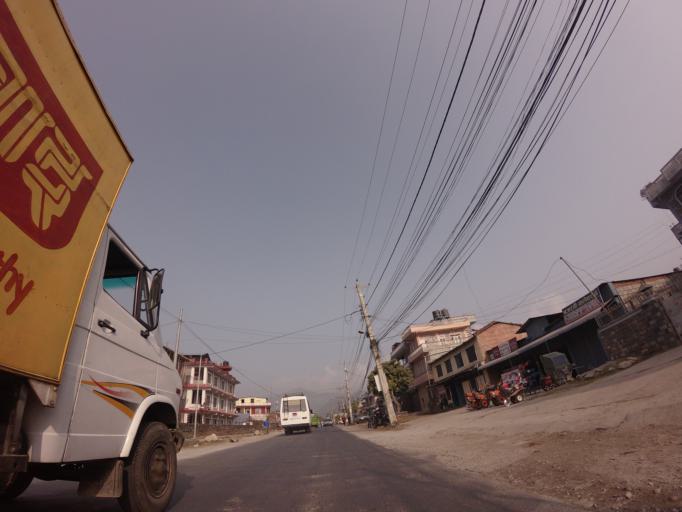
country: NP
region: Western Region
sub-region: Gandaki Zone
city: Pokhara
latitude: 28.1933
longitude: 83.9710
